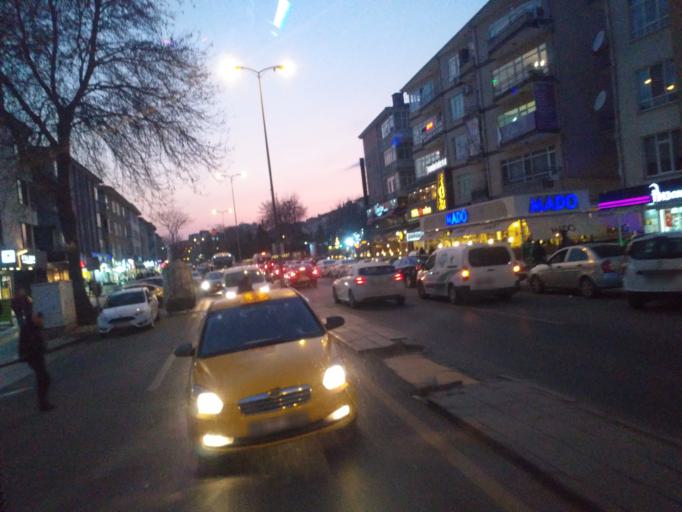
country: TR
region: Ankara
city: Ankara
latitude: 39.9723
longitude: 32.8404
